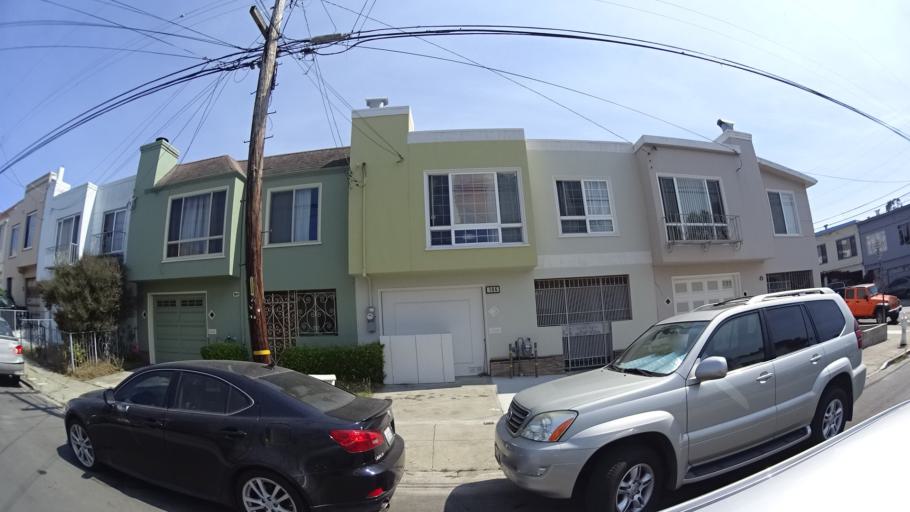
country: US
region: California
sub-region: San Mateo County
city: Daly City
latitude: 37.7127
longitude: -122.4635
